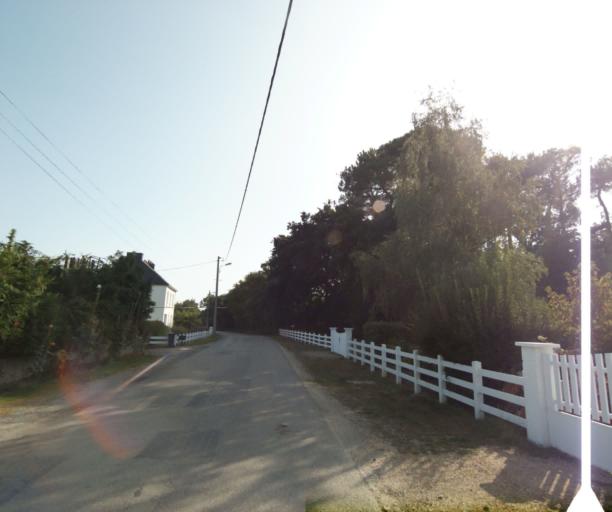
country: FR
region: Brittany
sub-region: Departement du Morbihan
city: Riantec
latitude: 47.7385
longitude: -3.2953
